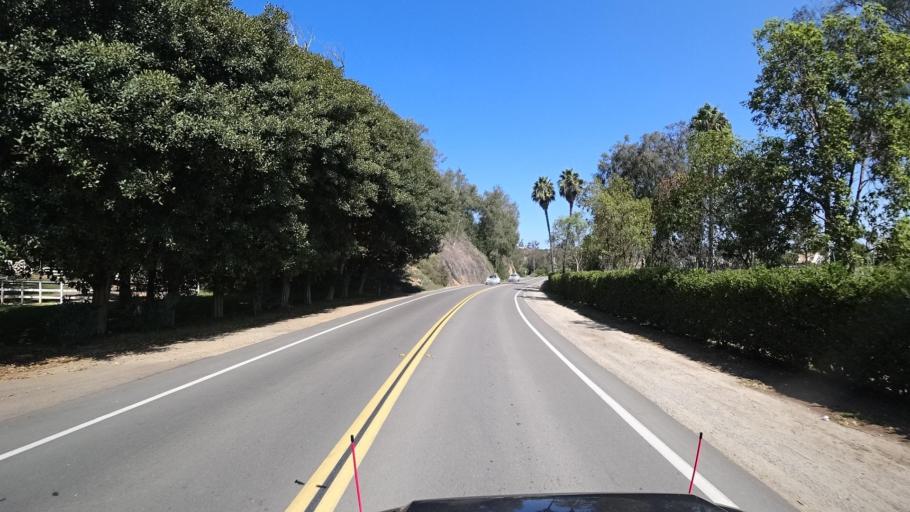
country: US
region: California
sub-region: San Diego County
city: Fairbanks Ranch
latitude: 32.9883
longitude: -117.2172
